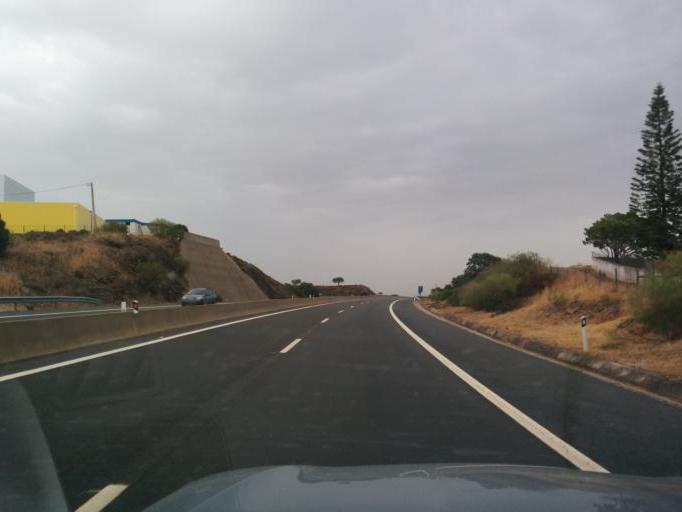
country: PT
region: Faro
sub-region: Tavira
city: Tavira
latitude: 37.1848
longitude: -7.5717
